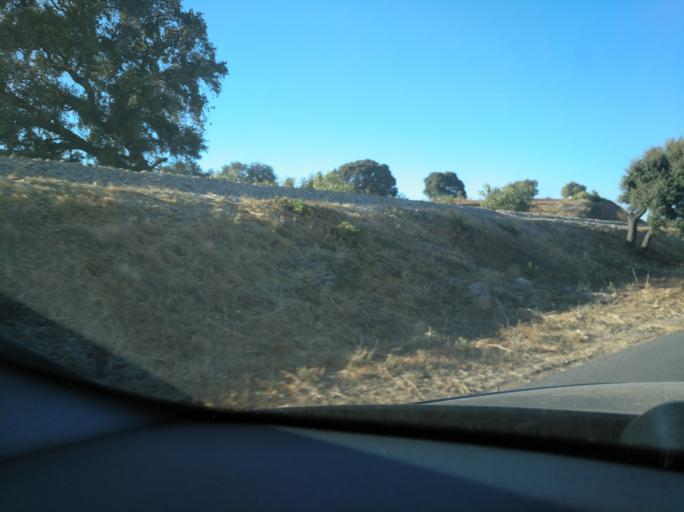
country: PT
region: Faro
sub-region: Vila Real de Santo Antonio
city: Monte Gordo
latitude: 37.1874
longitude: -7.5220
